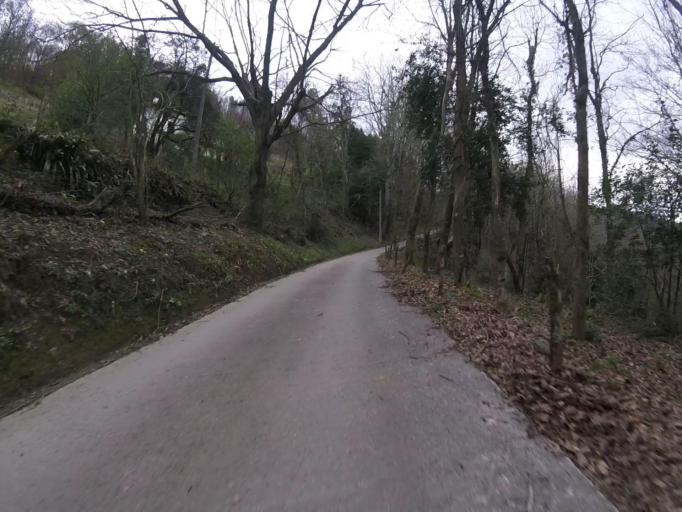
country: ES
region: Basque Country
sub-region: Provincia de Guipuzcoa
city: Errenteria
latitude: 43.2755
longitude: -1.8605
